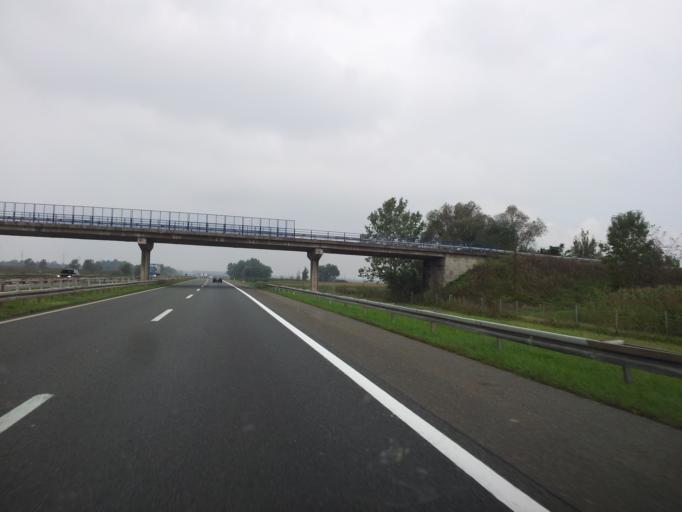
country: HR
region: Sisacko-Moslavacka
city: Repusnica
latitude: 45.4803
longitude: 16.7207
